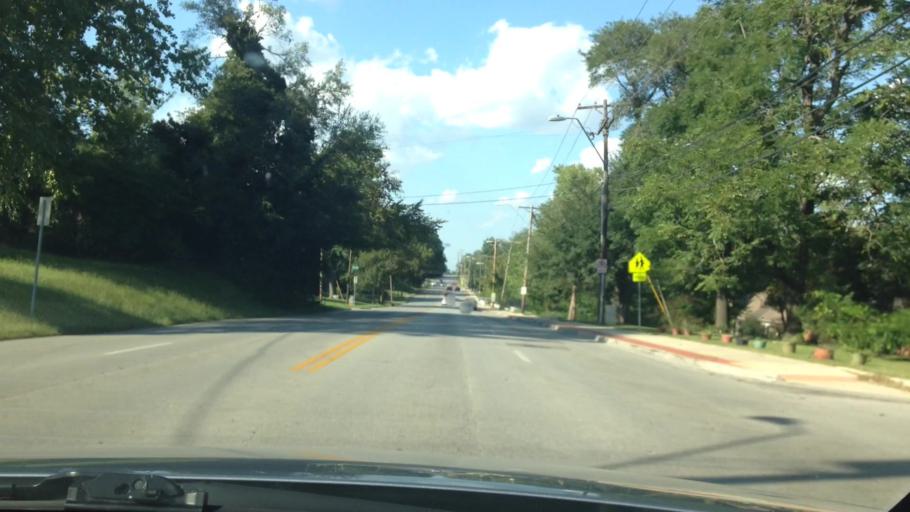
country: US
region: Kansas
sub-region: Johnson County
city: Leawood
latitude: 38.9628
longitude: -94.5817
